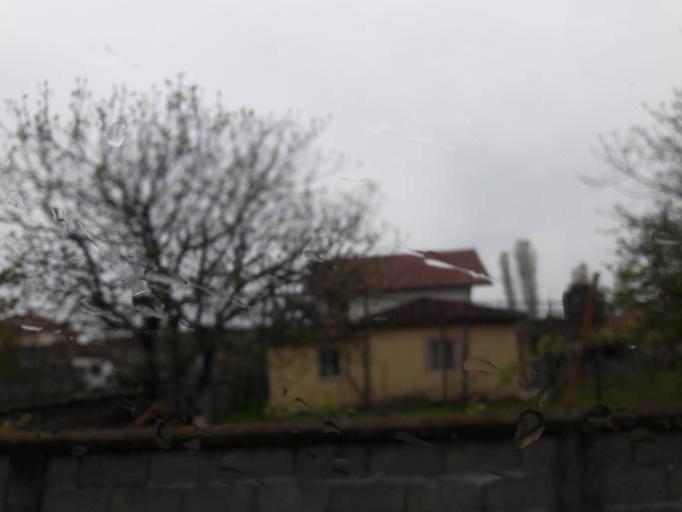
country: AL
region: Shkoder
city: Vukatane
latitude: 42.0158
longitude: 19.5424
